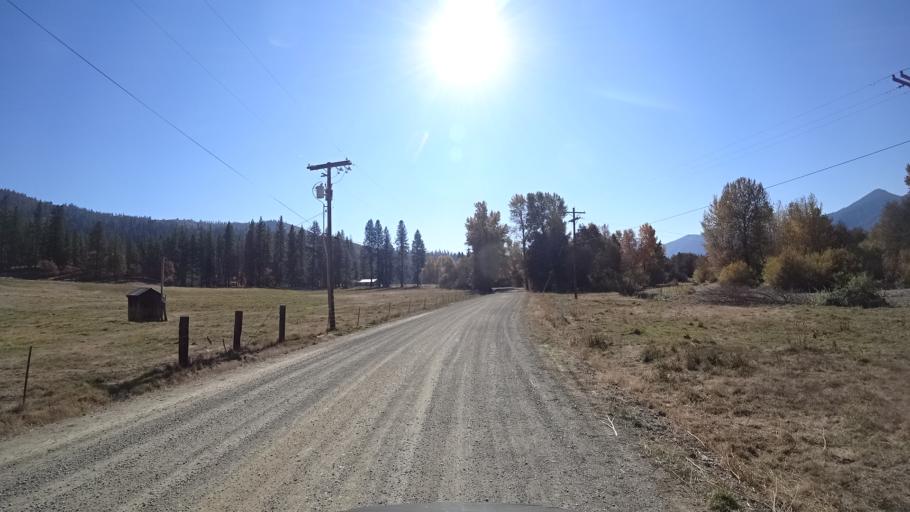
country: US
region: California
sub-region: Siskiyou County
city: Yreka
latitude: 41.6051
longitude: -122.9604
